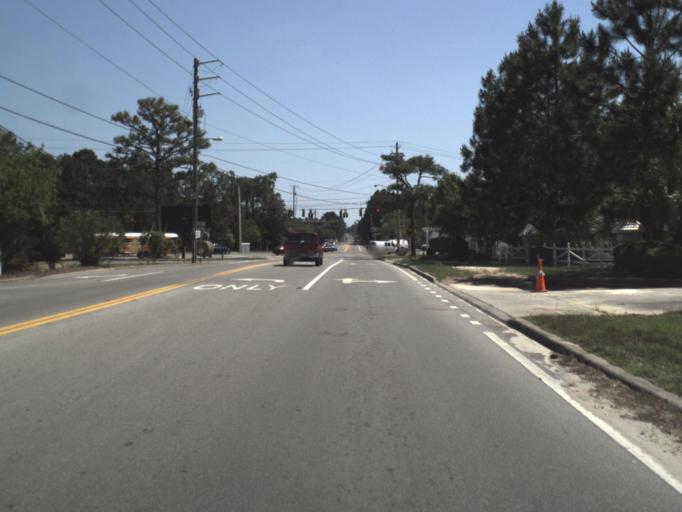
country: US
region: Florida
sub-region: Bay County
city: Hiland Park
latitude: 30.2146
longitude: -85.6075
